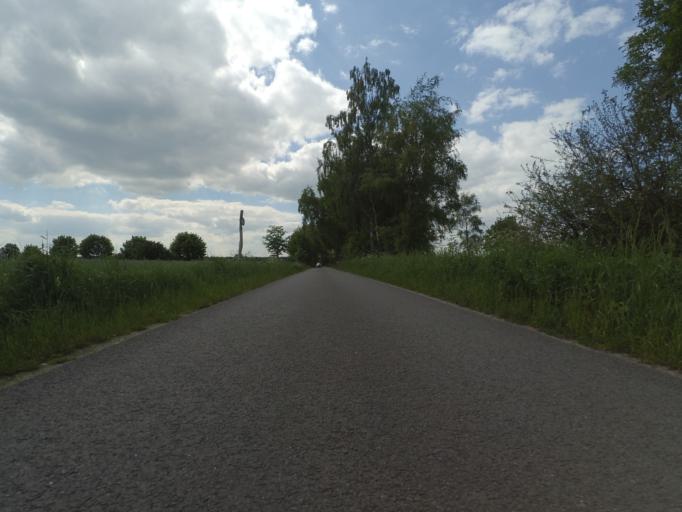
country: DE
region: Lower Saxony
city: Hohne
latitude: 52.6080
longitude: 10.3419
